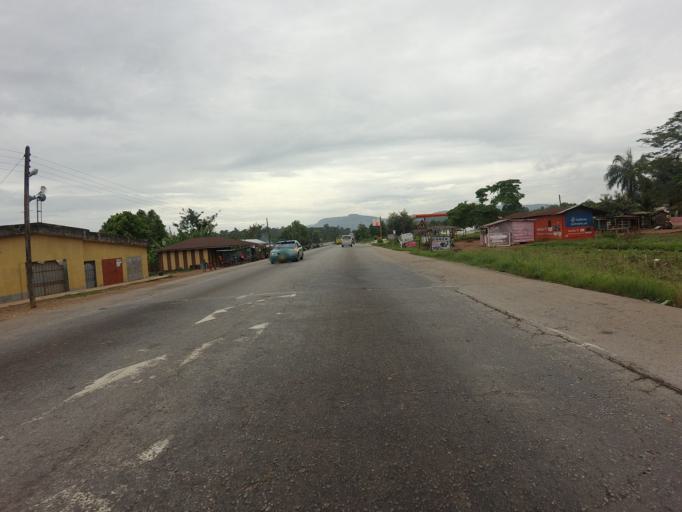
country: GH
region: Eastern
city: Nkawkaw
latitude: 6.4974
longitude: -0.6921
